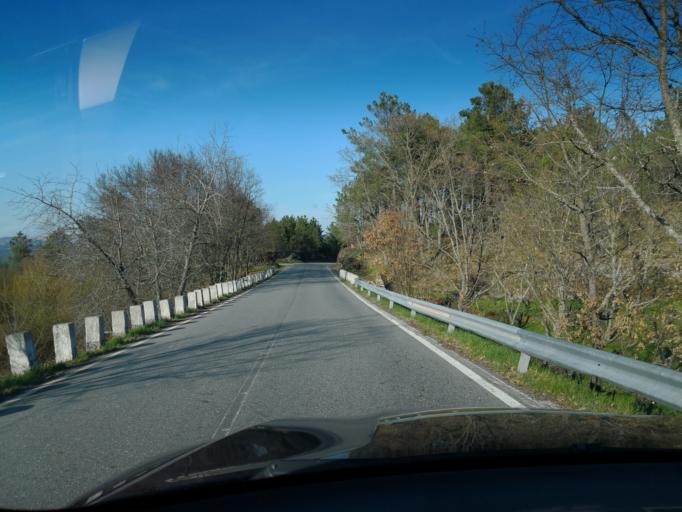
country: PT
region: Vila Real
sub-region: Sabrosa
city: Sabrosa
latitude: 41.3528
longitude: -7.6106
